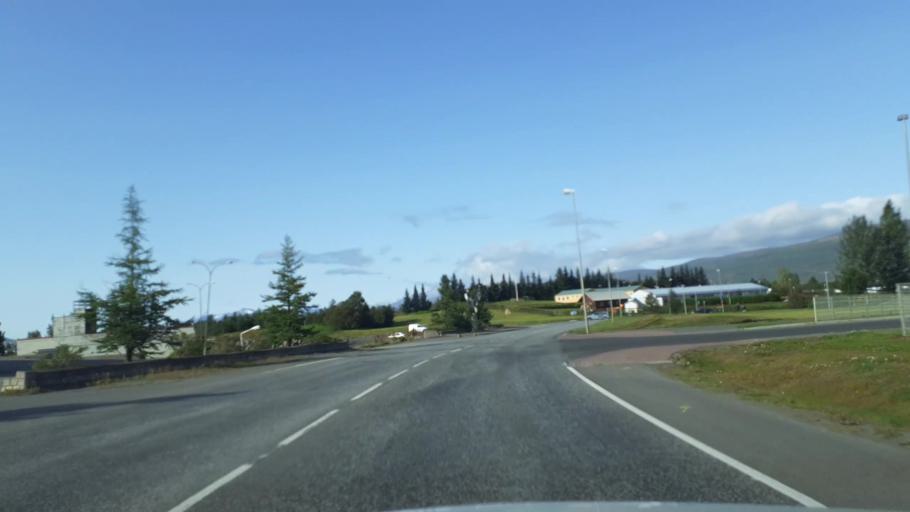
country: IS
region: Northeast
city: Akureyri
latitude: 65.6763
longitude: -18.1293
